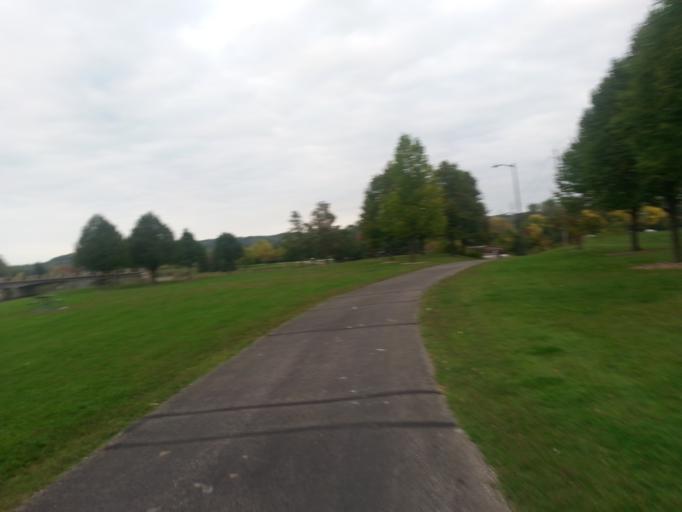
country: US
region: Minnesota
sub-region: Olmsted County
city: Rochester
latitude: 44.0286
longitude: -92.4575
